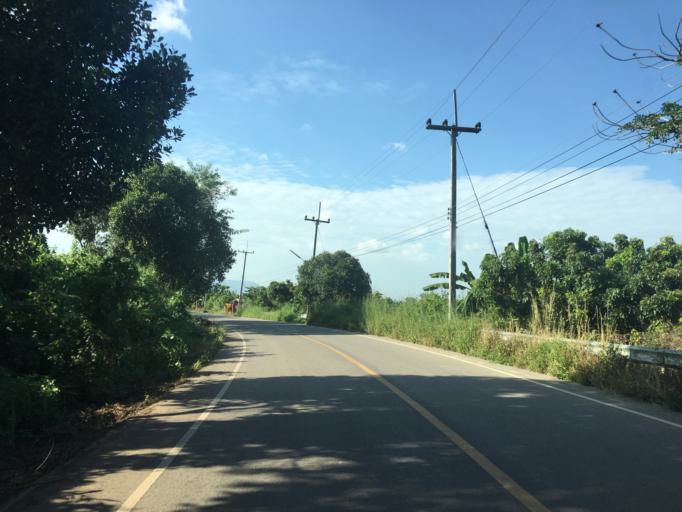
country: TH
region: Chiang Rai
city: Pa Daet
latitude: 19.4300
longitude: 100.0144
